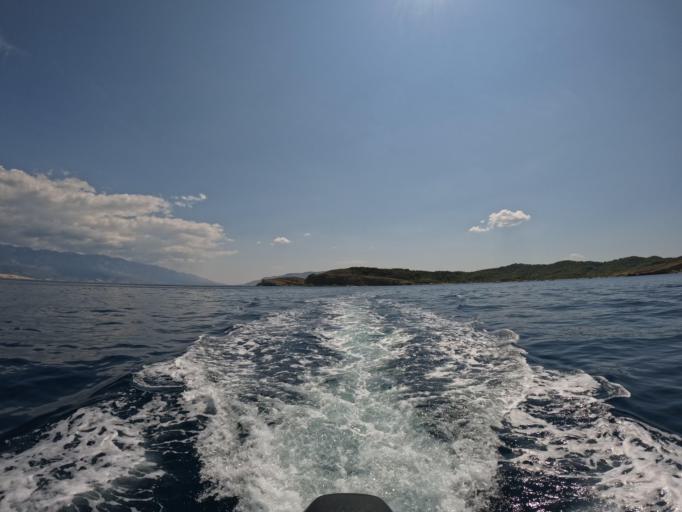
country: HR
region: Primorsko-Goranska
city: Lopar
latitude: 44.8479
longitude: 14.7575
